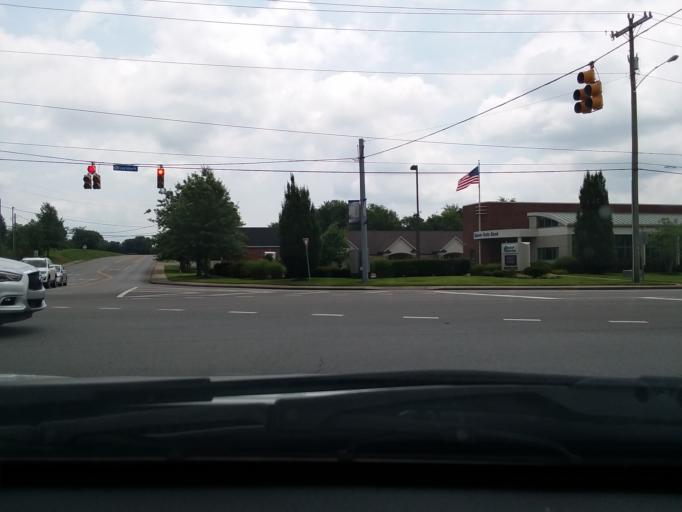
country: US
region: Tennessee
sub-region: Davidson County
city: Goodlettsville
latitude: 36.3296
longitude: -86.6978
